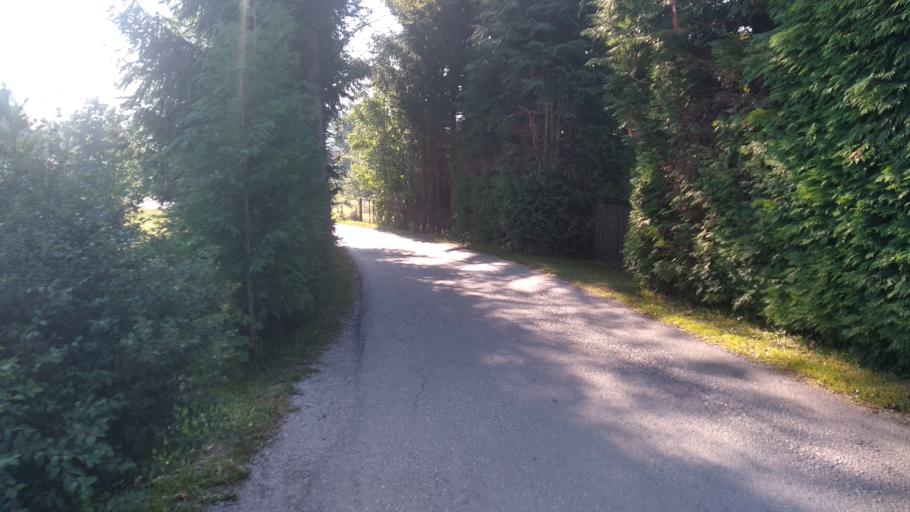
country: RS
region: Central Serbia
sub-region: Zlatiborski Okrug
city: Cajetina
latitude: 43.7355
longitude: 19.7191
